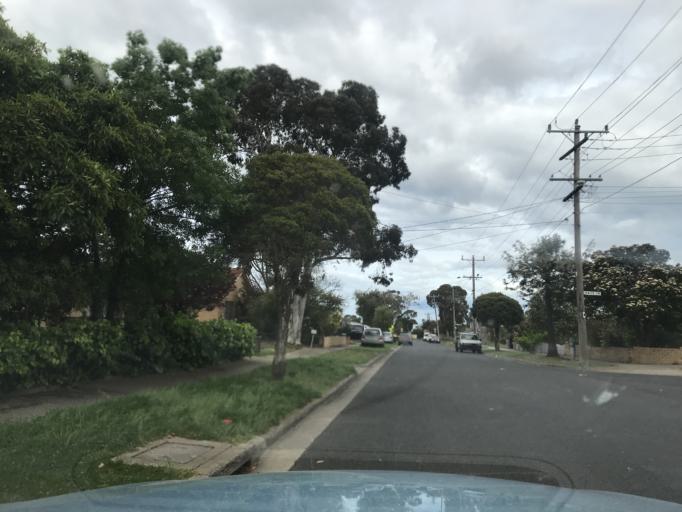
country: AU
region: Victoria
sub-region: Hobsons Bay
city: Laverton
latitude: -37.8502
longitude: 144.7723
